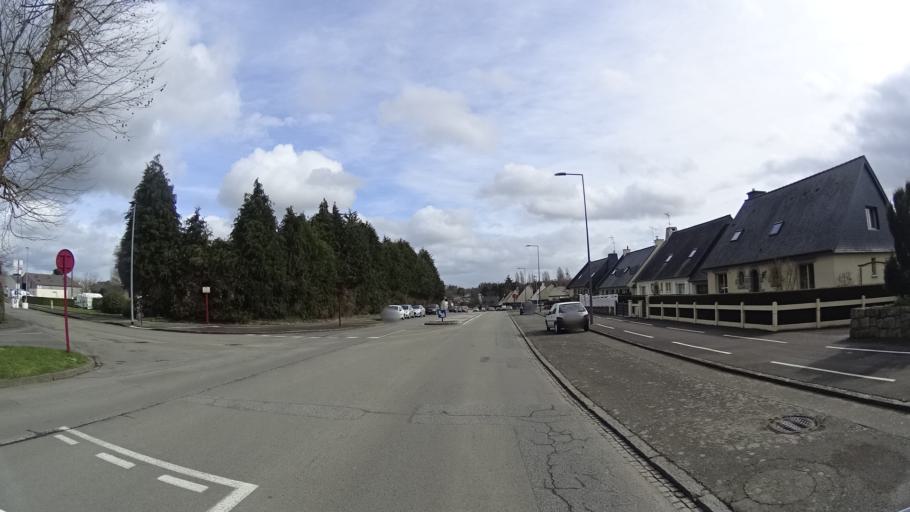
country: FR
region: Brittany
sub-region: Departement d'Ille-et-Vilaine
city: Saint-Gilles
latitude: 48.1551
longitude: -1.8231
